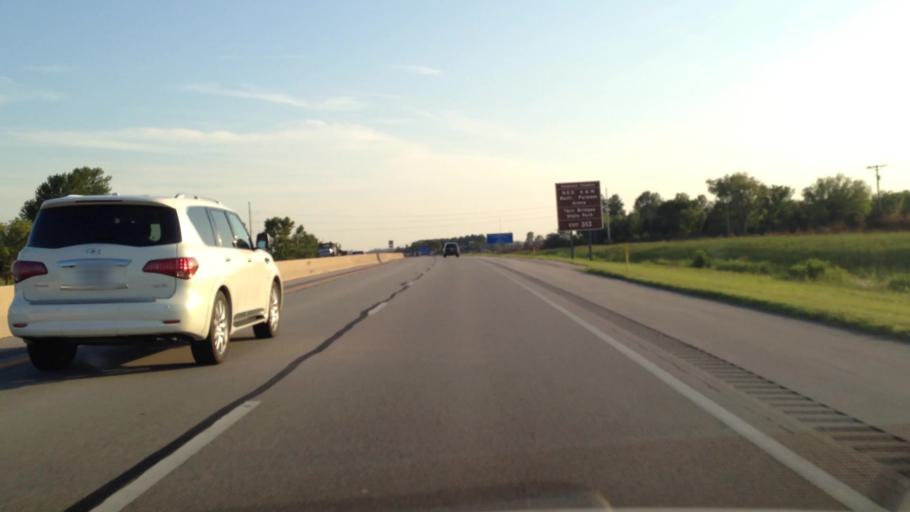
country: US
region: Oklahoma
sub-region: Ottawa County
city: Miami
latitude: 36.8811
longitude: -94.8425
